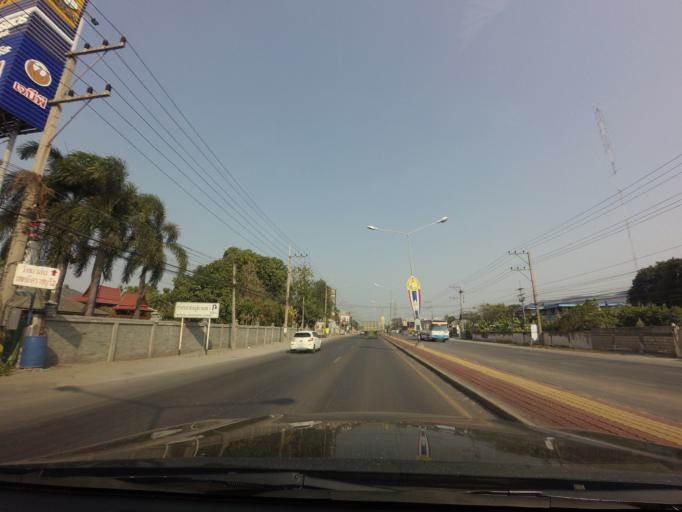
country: TH
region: Ratchaburi
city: Ban Pong
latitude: 13.8483
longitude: 99.8537
